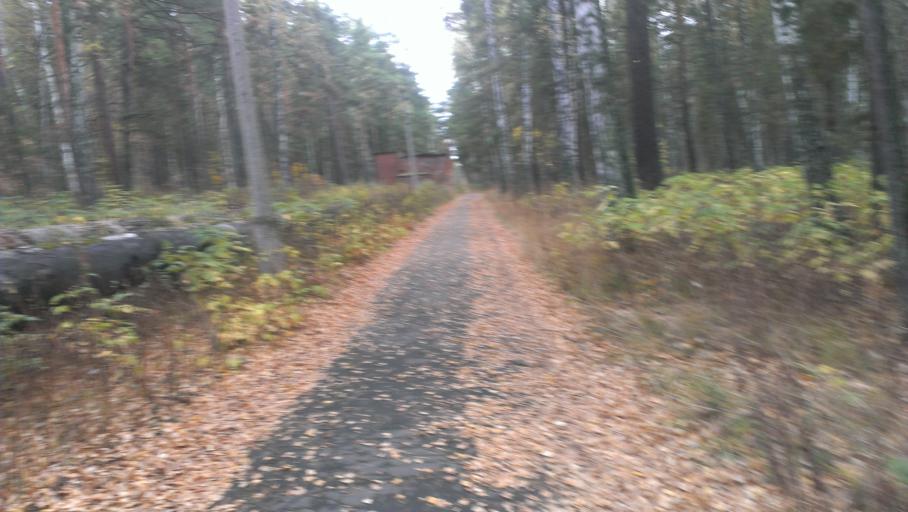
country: RU
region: Altai Krai
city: Yuzhnyy
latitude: 53.2702
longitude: 83.6809
